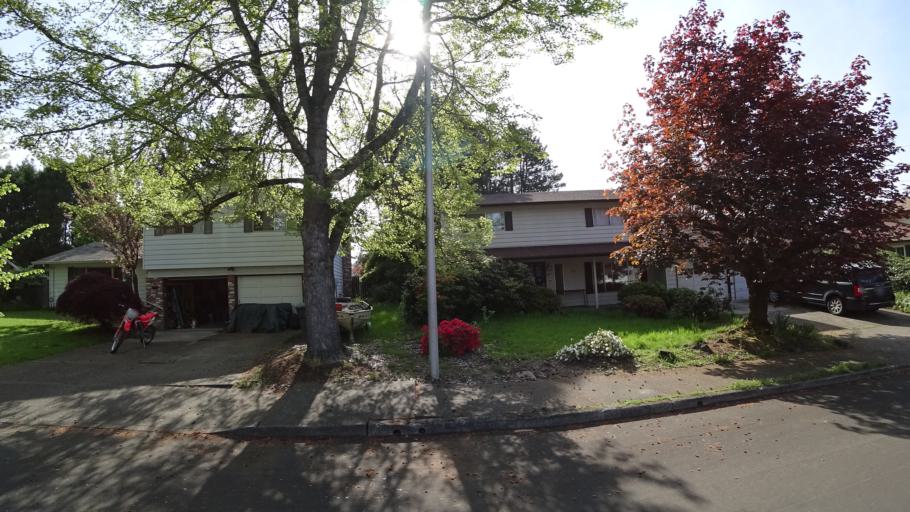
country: US
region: Oregon
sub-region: Washington County
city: Hillsboro
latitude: 45.5229
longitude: -122.9613
